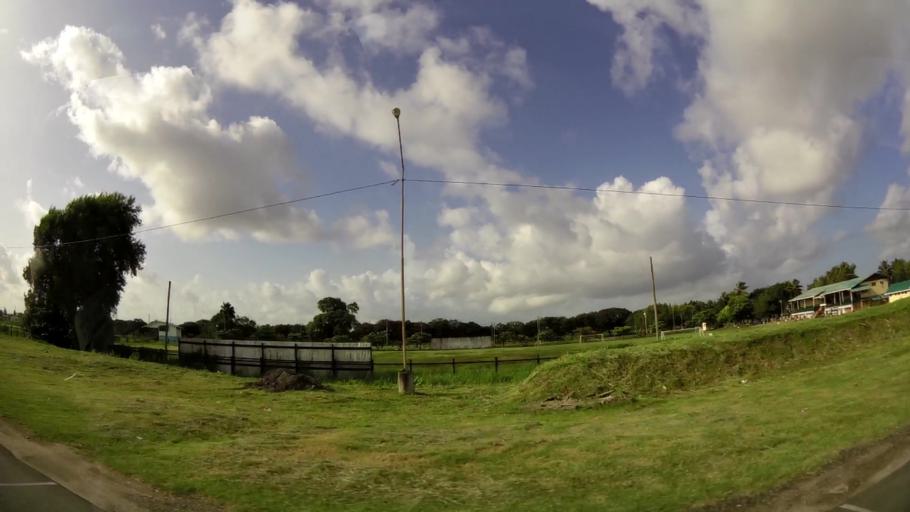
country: GY
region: Demerara-Mahaica
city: Georgetown
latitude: 6.8249
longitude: -58.1508
